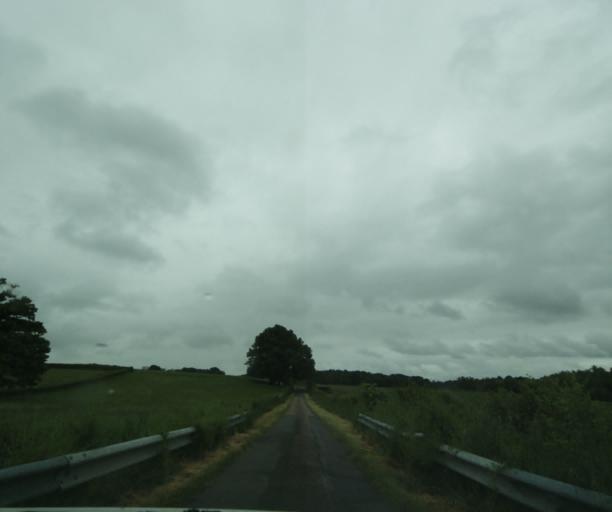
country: FR
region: Bourgogne
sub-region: Departement de Saone-et-Loire
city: Palinges
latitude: 46.4930
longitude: 4.2365
